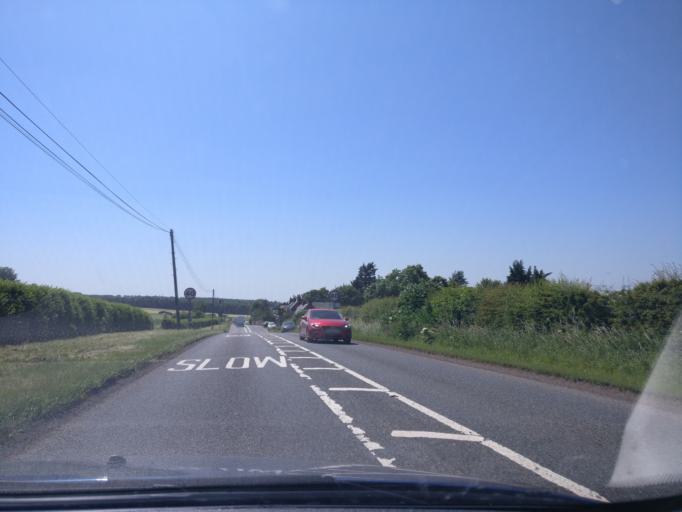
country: GB
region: Scotland
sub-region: East Lothian
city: Gullane
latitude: 55.9944
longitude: -2.8282
